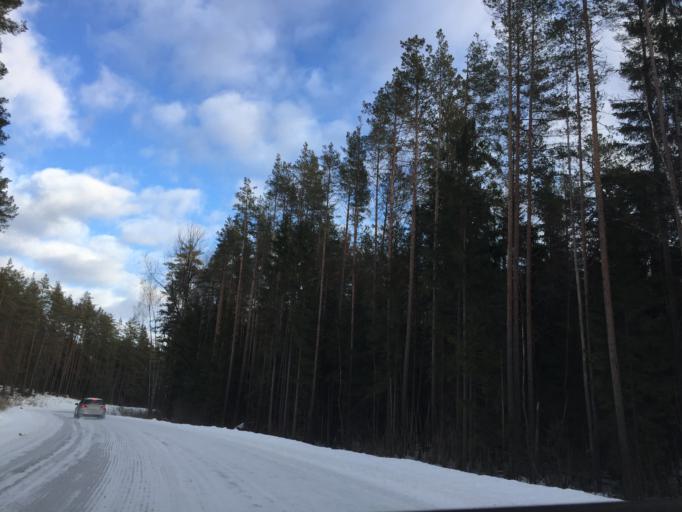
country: LV
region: Ogre
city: Jumprava
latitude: 56.5759
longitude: 24.9418
